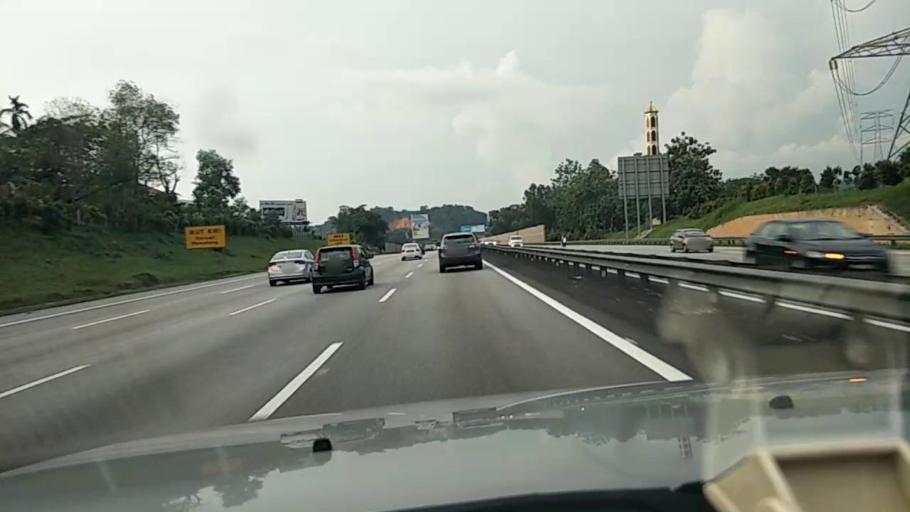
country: MY
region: Selangor
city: Kuang
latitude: 3.2426
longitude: 101.5654
